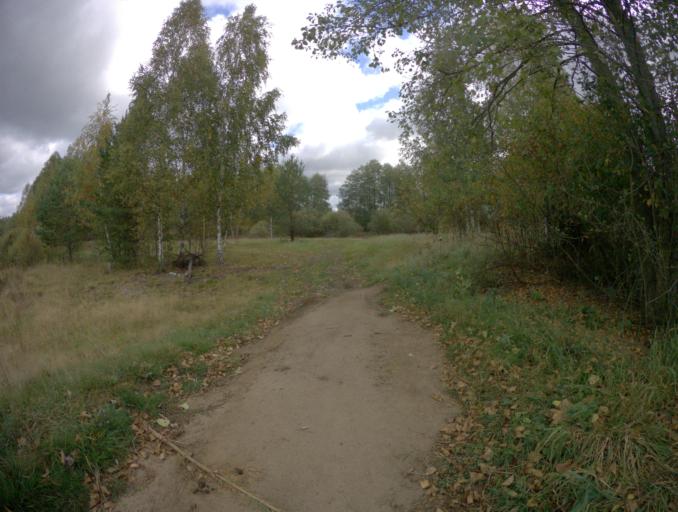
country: RU
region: Moskovskaya
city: Baksheyevo
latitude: 55.7155
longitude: 39.8551
